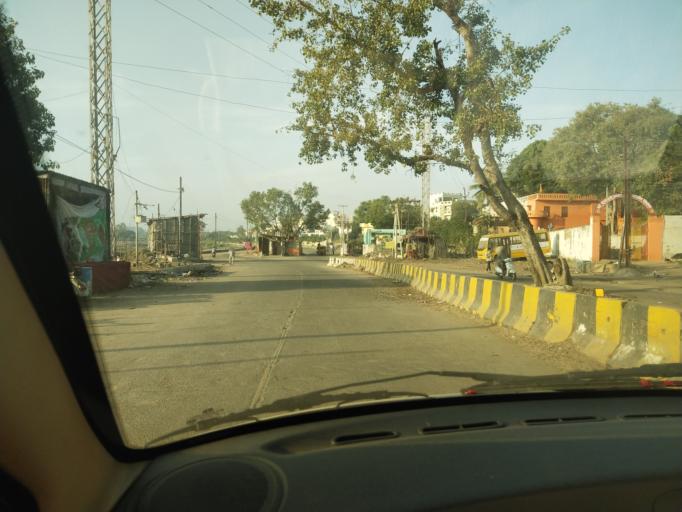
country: IN
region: Telangana
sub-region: Hyderabad
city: Hyderabad
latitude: 17.3680
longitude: 78.4574
